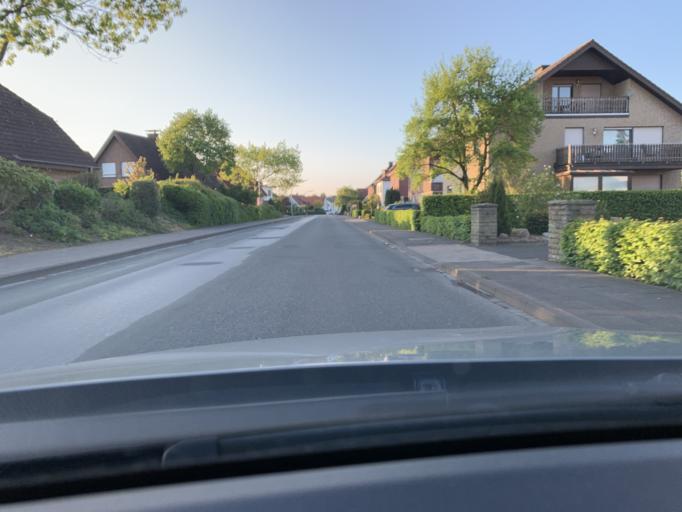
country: DE
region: North Rhine-Westphalia
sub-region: Regierungsbezirk Detmold
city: Rheda-Wiedenbruck
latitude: 51.8358
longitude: 8.3225
